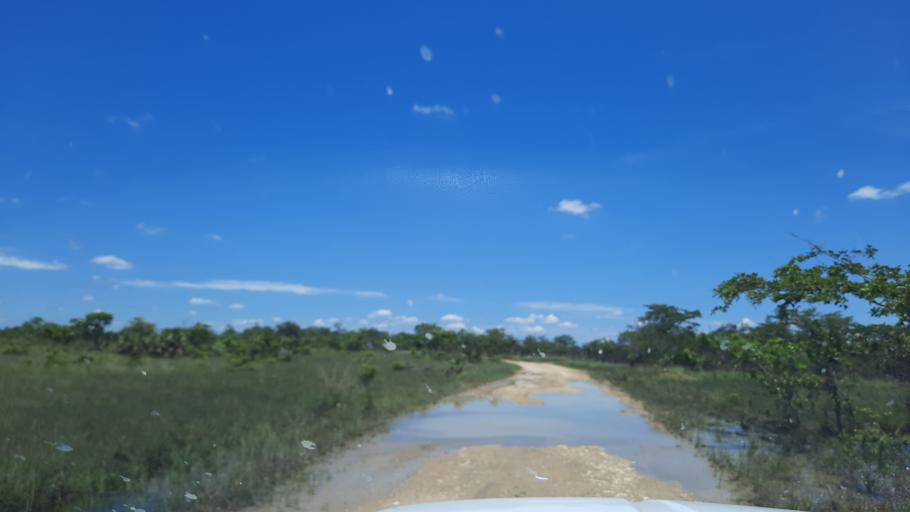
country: BZ
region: Cayo
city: Belmopan
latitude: 17.3840
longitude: -88.4943
